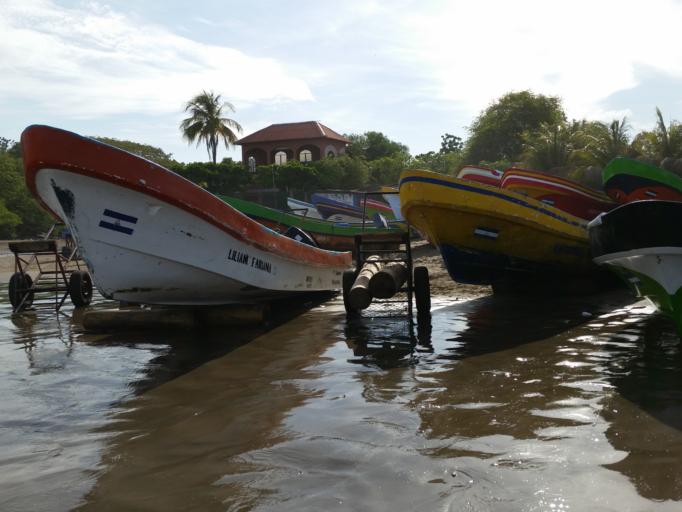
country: NI
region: Managua
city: Masachapa
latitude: 11.7865
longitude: -86.5166
